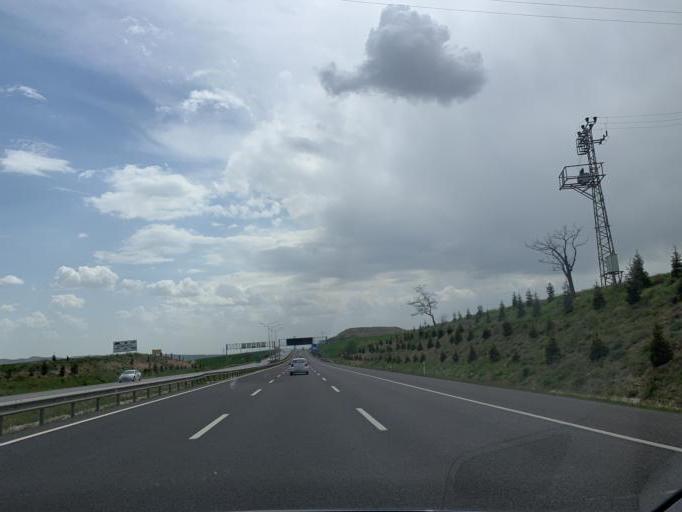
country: TR
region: Ankara
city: Polatli
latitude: 39.5996
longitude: 32.1771
